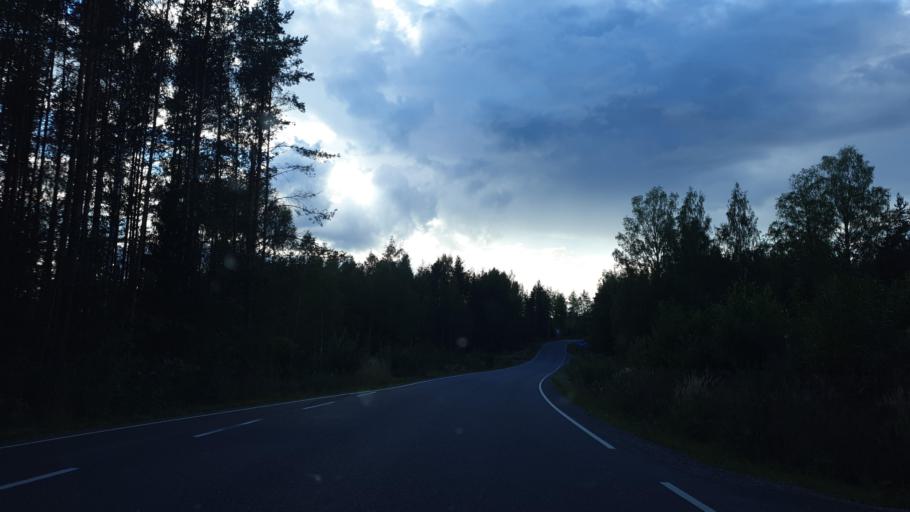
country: FI
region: Northern Savo
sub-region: Koillis-Savo
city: Juankoski
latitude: 63.2022
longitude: 28.2872
